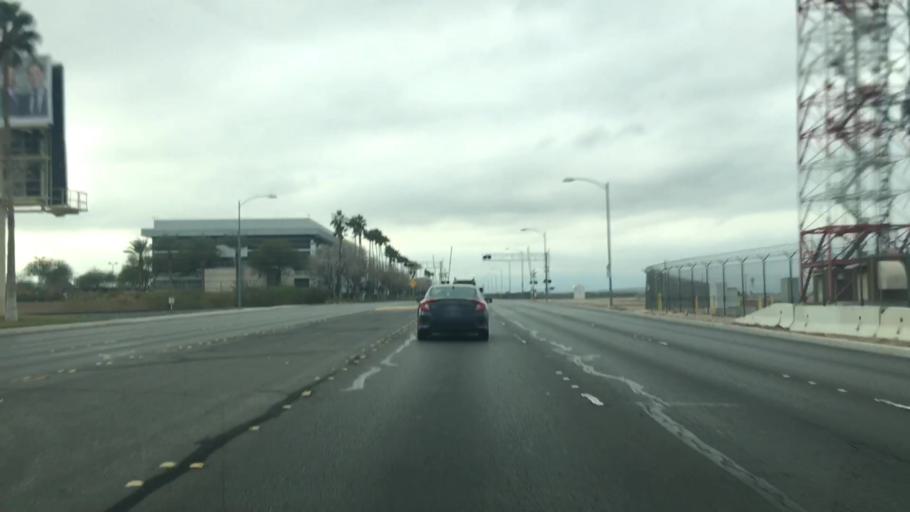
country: US
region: Nevada
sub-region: Clark County
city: Paradise
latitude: 36.0714
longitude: -115.1565
